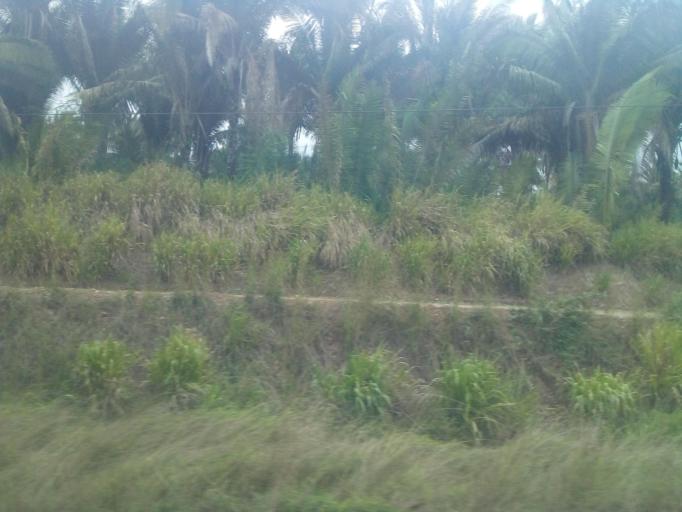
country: BR
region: Maranhao
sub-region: Pindare Mirim
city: Pindare Mirim
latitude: -3.6431
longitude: -45.2207
